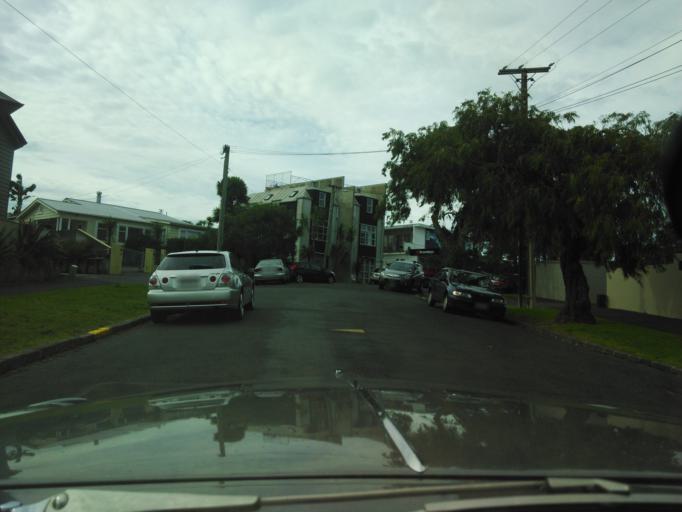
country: NZ
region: Auckland
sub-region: Auckland
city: Rosebank
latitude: -36.8595
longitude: 174.7013
